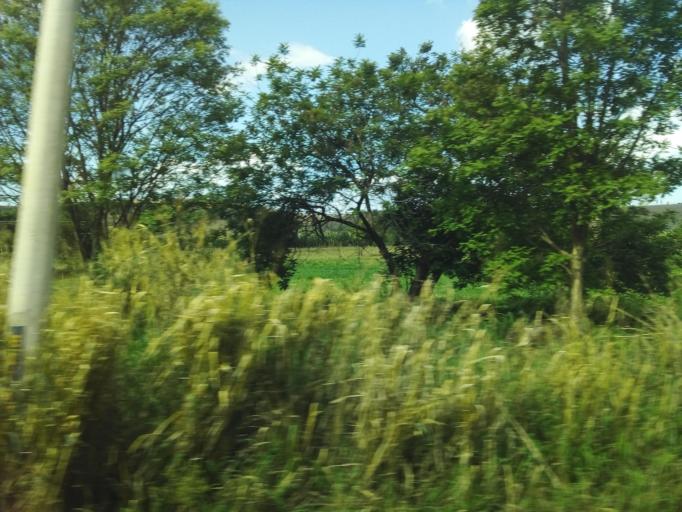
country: BR
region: Minas Gerais
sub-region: Conselheiro Pena
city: Conselheiro Pena
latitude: -18.9863
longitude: -41.6020
